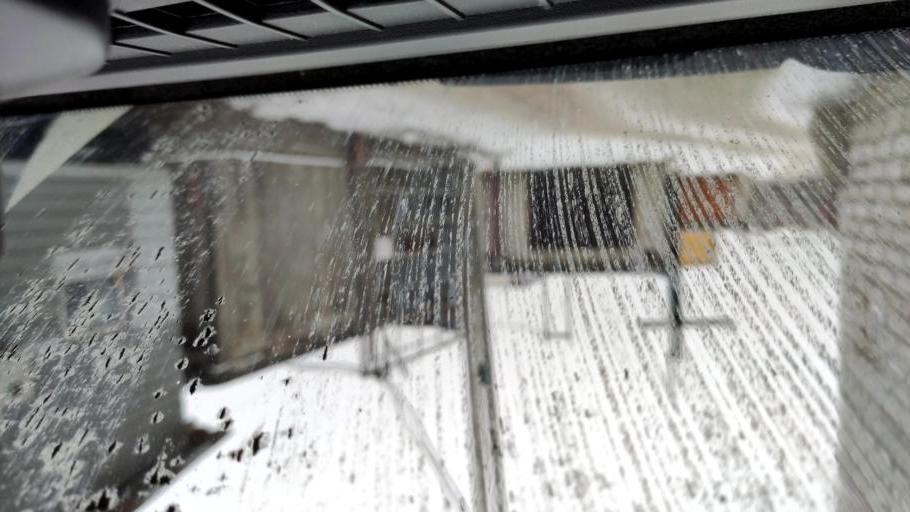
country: RU
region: Perm
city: Froly
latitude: 57.9549
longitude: 56.2278
